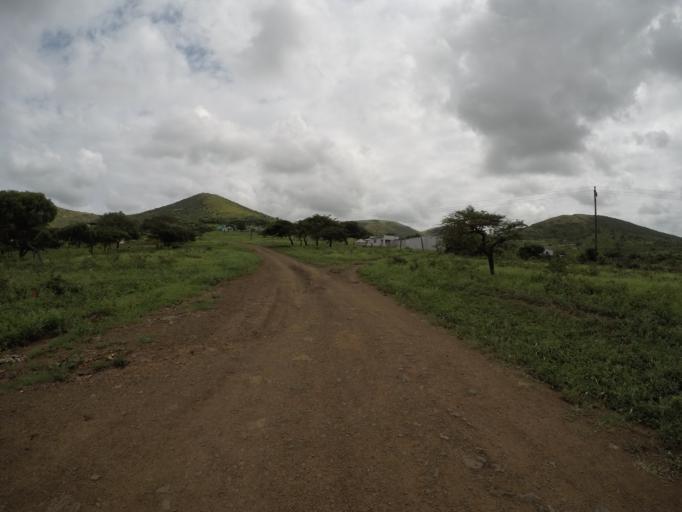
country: ZA
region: KwaZulu-Natal
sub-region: uThungulu District Municipality
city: Empangeni
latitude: -28.5910
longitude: 31.8897
